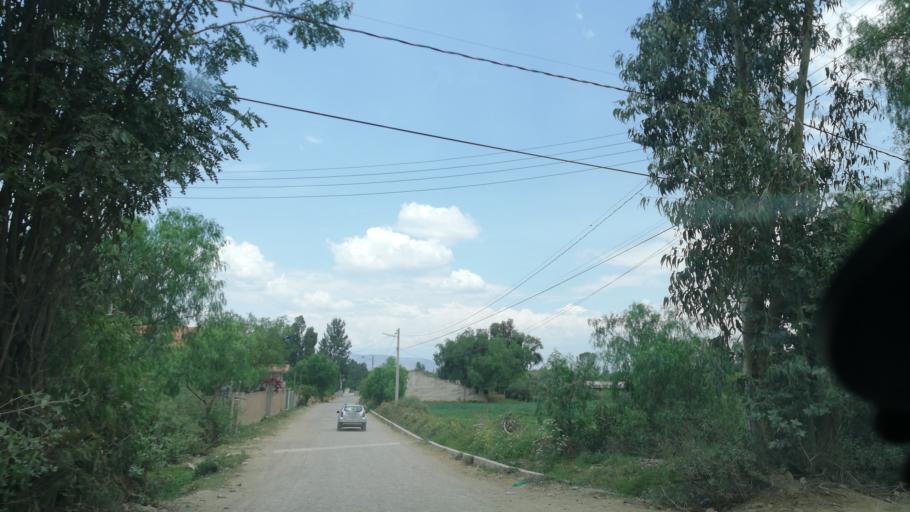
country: BO
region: Cochabamba
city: Cochabamba
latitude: -17.3559
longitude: -66.2206
